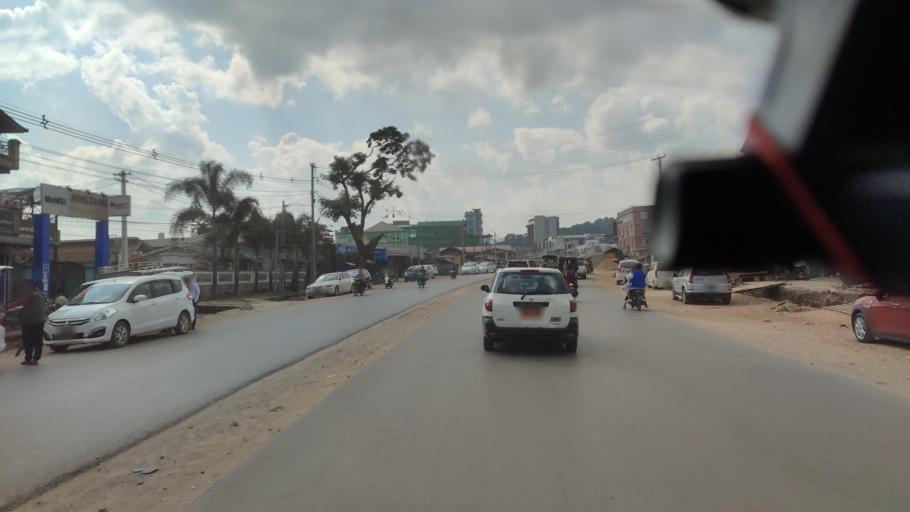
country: MM
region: Shan
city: Lashio
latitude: 22.9535
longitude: 97.7610
